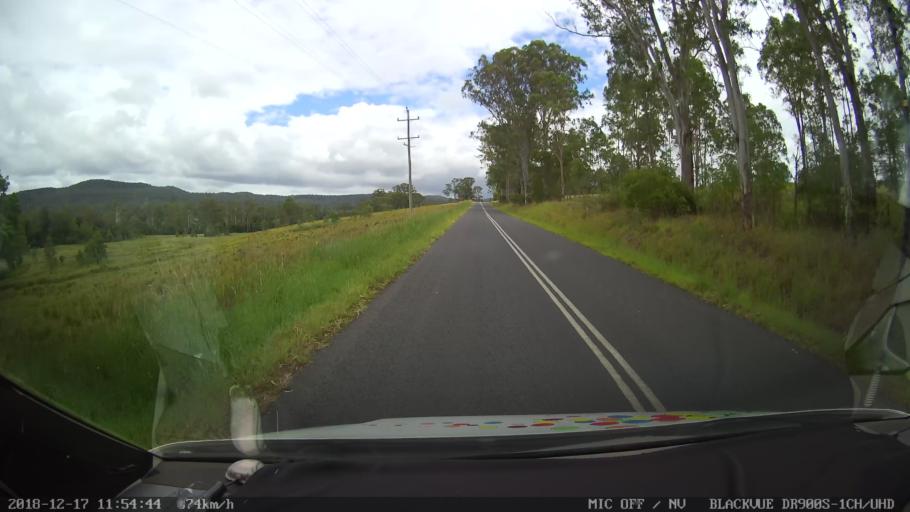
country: AU
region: New South Wales
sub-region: Kyogle
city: Kyogle
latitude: -28.5632
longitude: 152.5820
